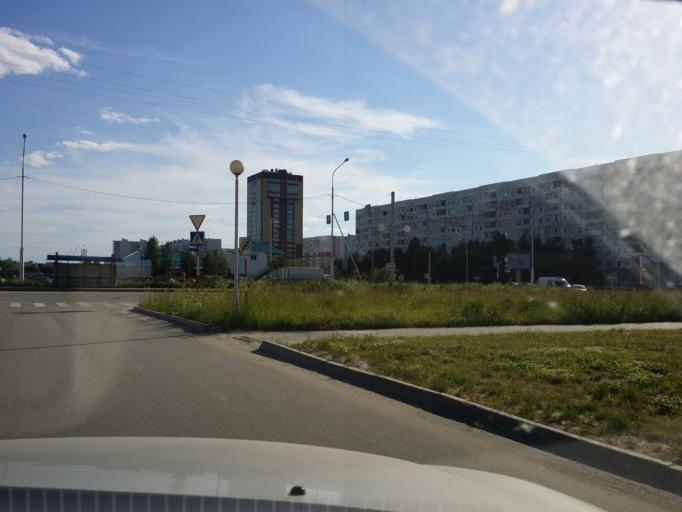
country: RU
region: Khanty-Mansiyskiy Avtonomnyy Okrug
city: Nizhnevartovsk
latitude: 60.9288
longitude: 76.6078
